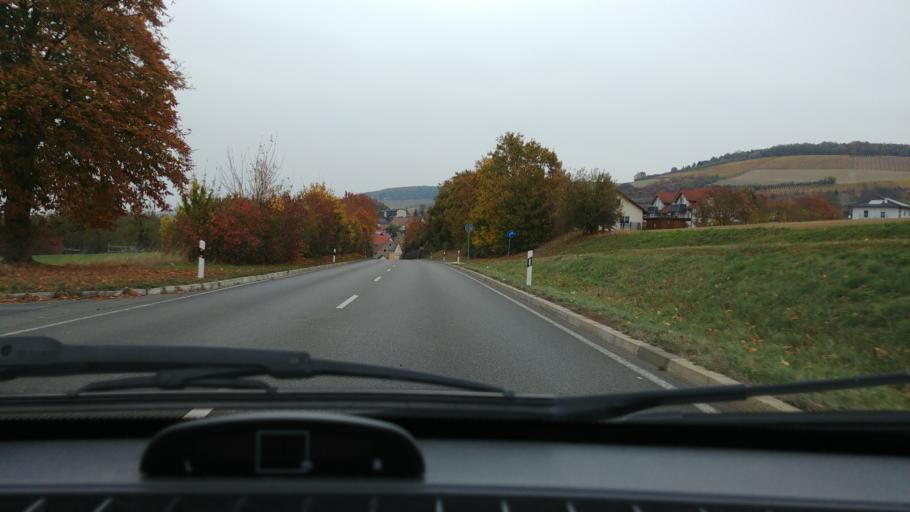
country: DE
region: Baden-Wuerttemberg
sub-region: Regierungsbezirk Stuttgart
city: Bad Mergentheim
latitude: 49.5240
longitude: 9.7484
